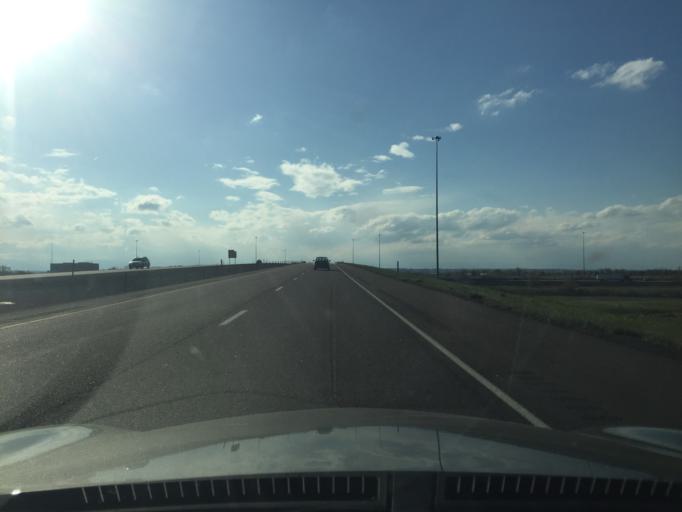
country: US
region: Colorado
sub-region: Adams County
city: Brighton
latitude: 39.9232
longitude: -104.7987
